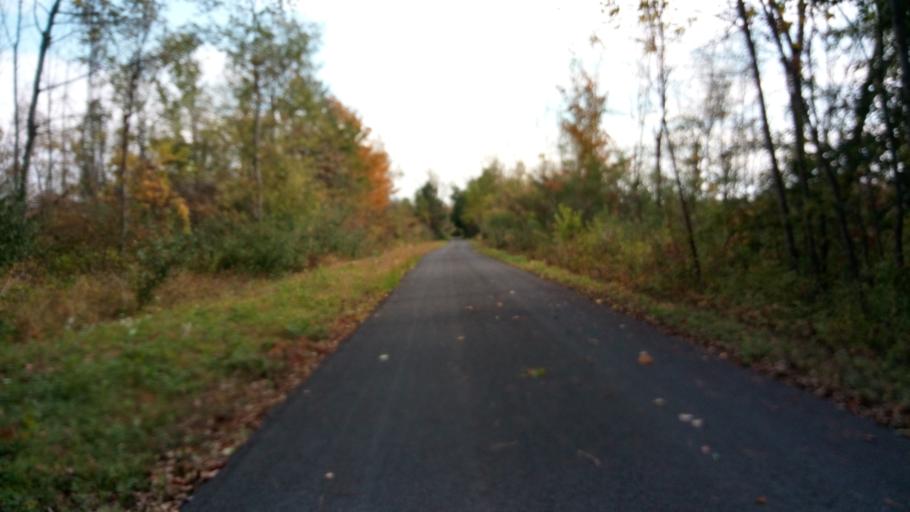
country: US
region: New York
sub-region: Wayne County
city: Clyde
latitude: 43.0726
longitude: -76.8598
